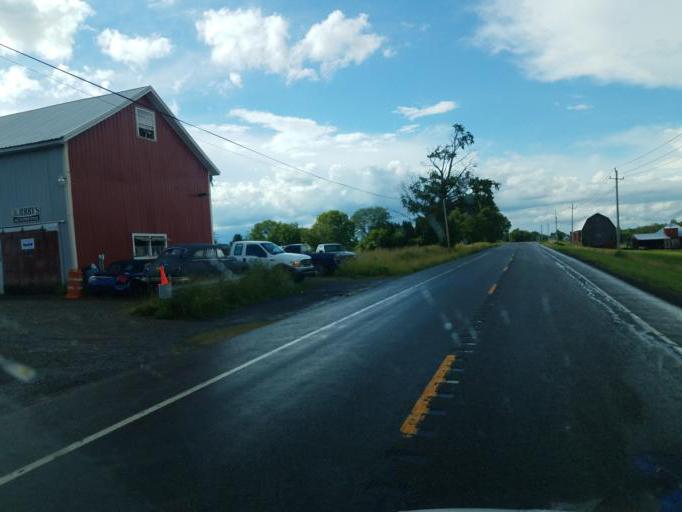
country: US
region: New York
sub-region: Seneca County
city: Waterloo
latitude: 42.9834
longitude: -76.8508
